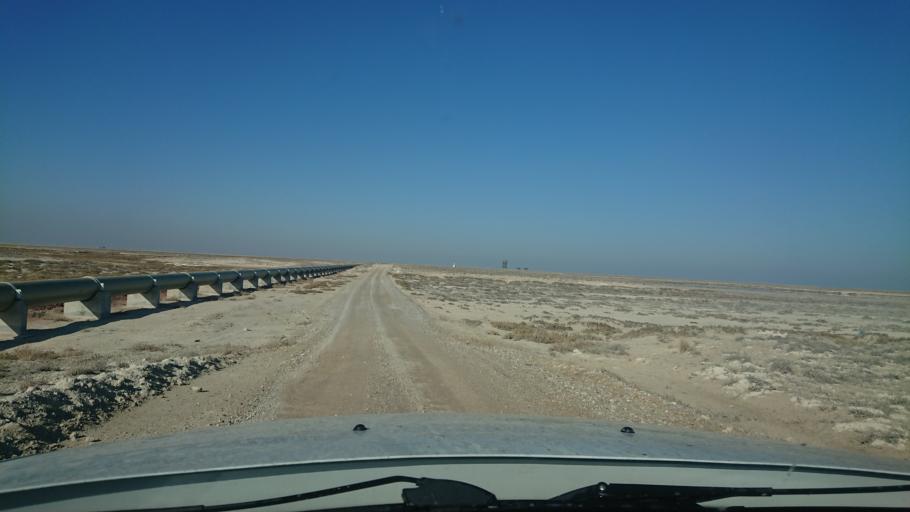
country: TR
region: Aksaray
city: Eskil
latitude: 38.4191
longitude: 33.5029
